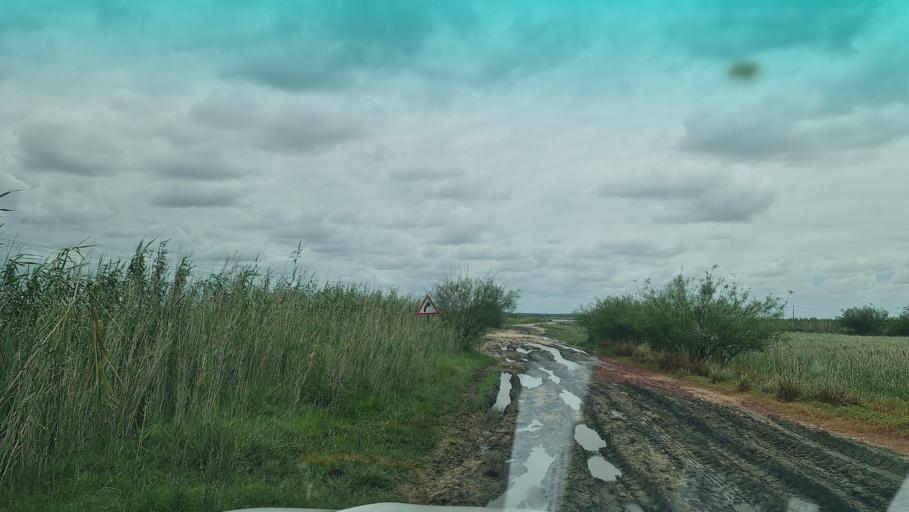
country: MZ
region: Maputo City
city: Maputo
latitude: -25.7245
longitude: 32.7002
